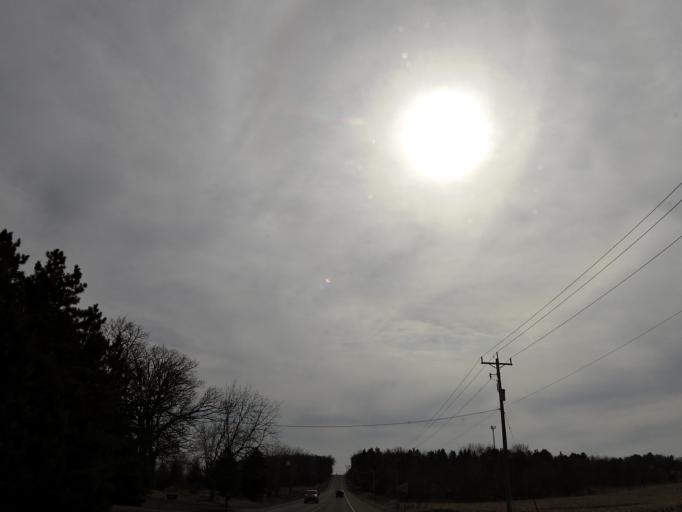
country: US
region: Minnesota
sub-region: Washington County
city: Lake Elmo
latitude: 44.9335
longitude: -92.8627
